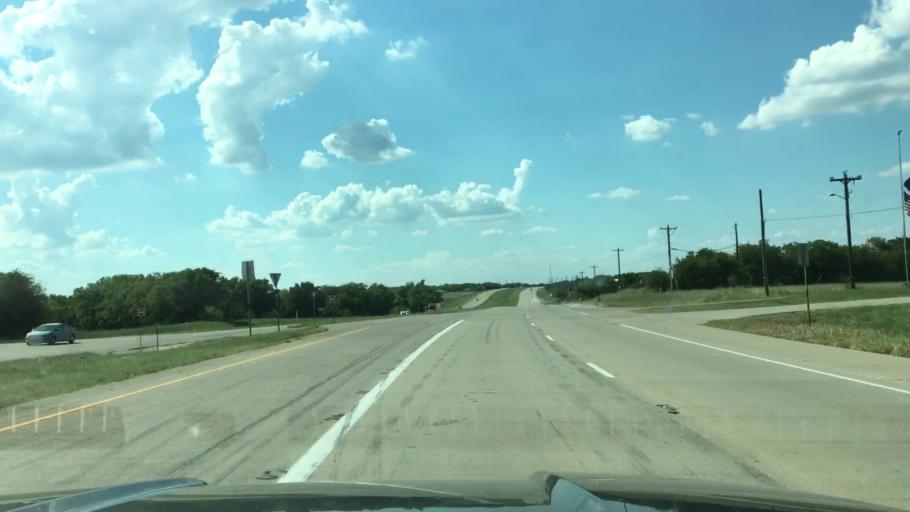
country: US
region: Texas
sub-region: Wise County
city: Rhome
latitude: 33.0382
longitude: -97.4423
